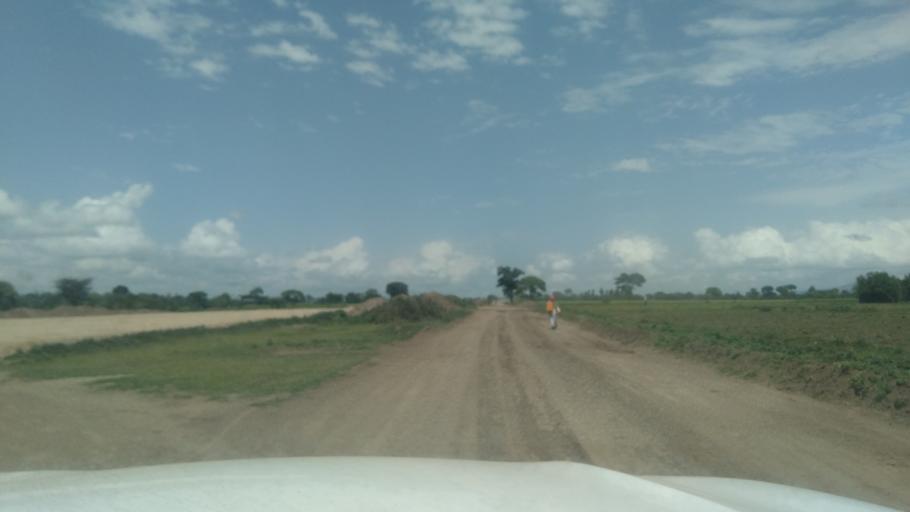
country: ET
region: Oromiya
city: Shashemene
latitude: 7.2762
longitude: 38.6024
